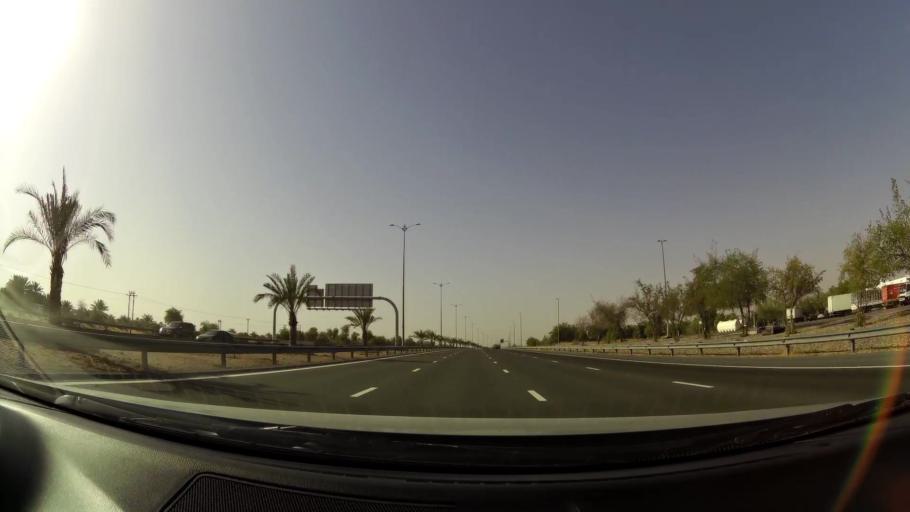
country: OM
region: Al Buraimi
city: Al Buraymi
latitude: 24.5606
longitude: 55.7519
